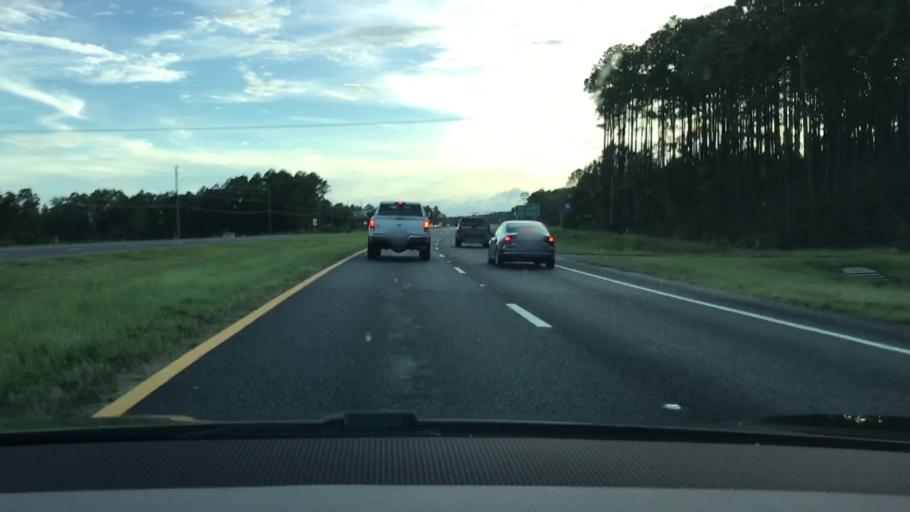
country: US
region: Florida
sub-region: Walton County
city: Freeport
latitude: 30.4449
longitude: -86.1345
